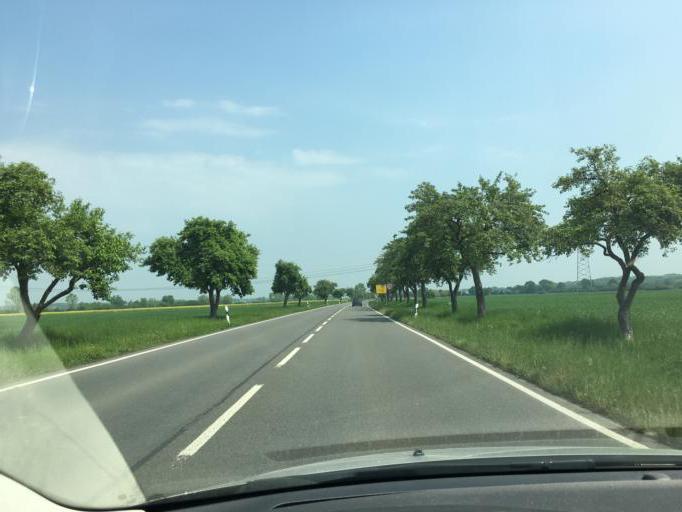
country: DE
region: Saxony
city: Naunhof
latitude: 51.2716
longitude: 12.5551
